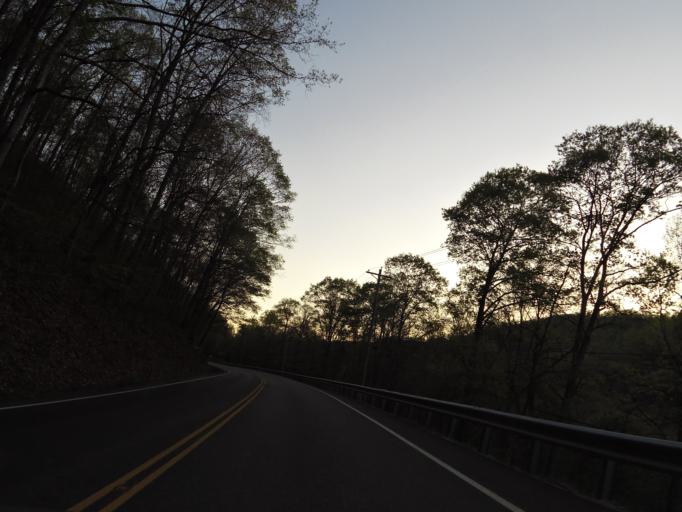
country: US
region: Tennessee
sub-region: Campbell County
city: LaFollette
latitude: 36.4101
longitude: -84.1040
